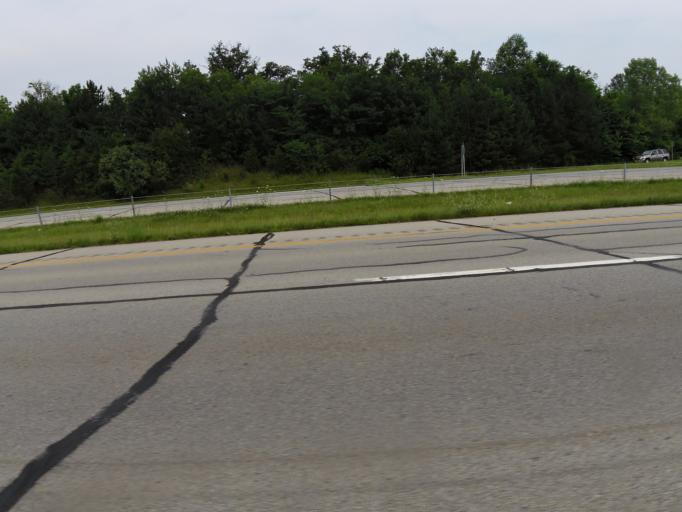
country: US
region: Ohio
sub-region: Montgomery County
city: Centerville
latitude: 39.6423
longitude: -84.1651
